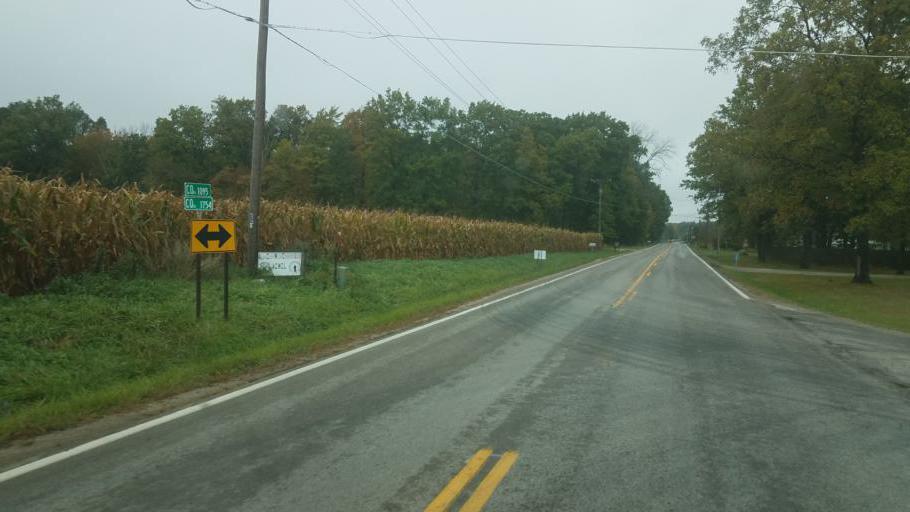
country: US
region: Ohio
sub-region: Ashland County
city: Ashland
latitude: 40.8060
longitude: -82.3398
